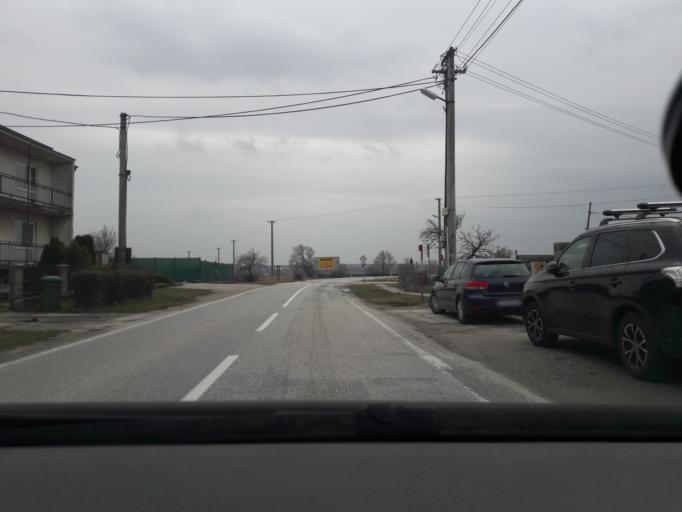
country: SK
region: Trnavsky
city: Smolenice
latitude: 48.4113
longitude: 17.3805
